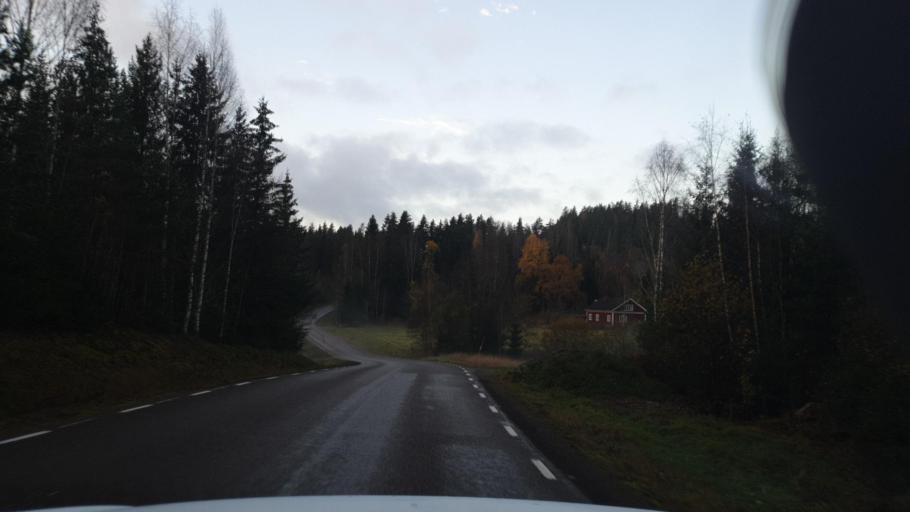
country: SE
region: Vaermland
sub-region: Arvika Kommun
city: Arvika
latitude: 59.6179
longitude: 12.7876
